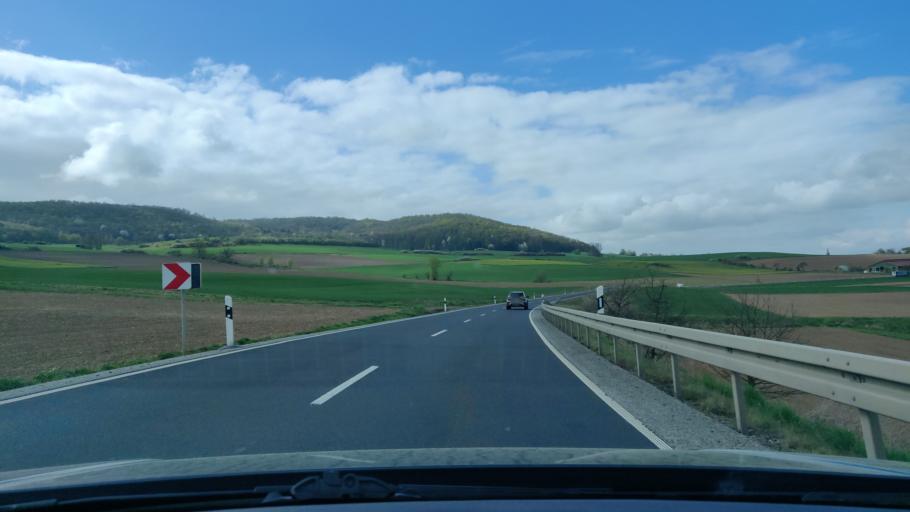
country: DE
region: Hesse
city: Felsberg
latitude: 51.1089
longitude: 9.4048
